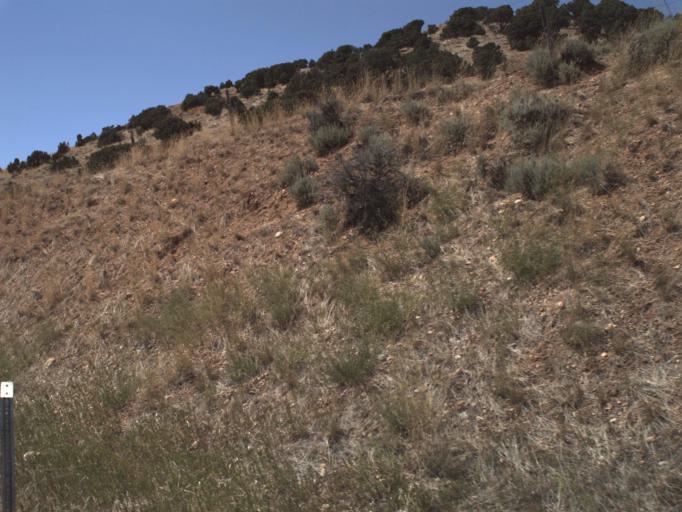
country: US
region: Utah
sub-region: Rich County
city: Randolph
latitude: 41.5102
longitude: -111.2259
